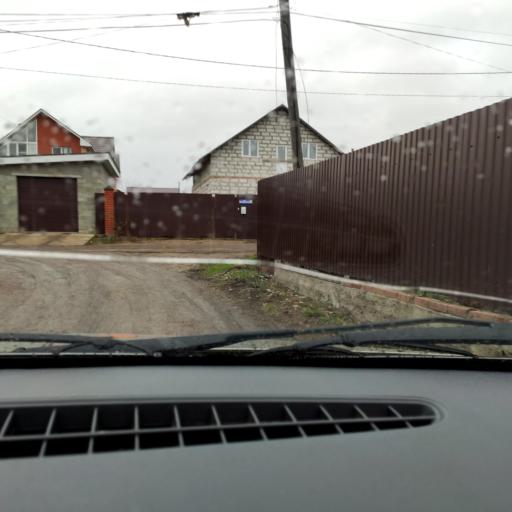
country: RU
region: Bashkortostan
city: Ufa
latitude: 54.6089
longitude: 55.9481
